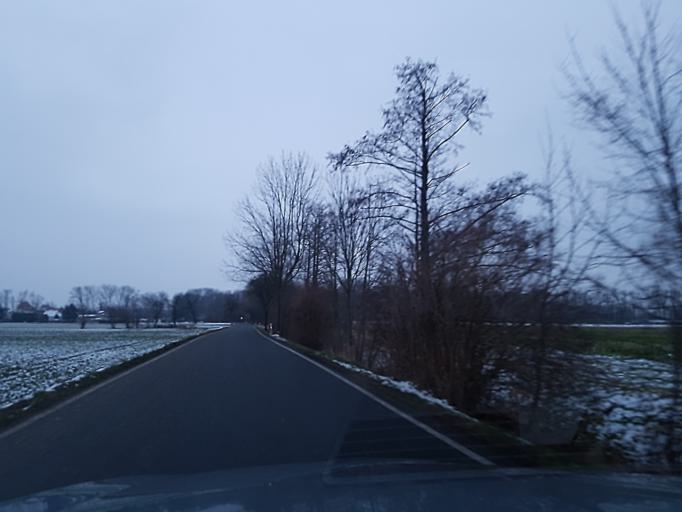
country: DE
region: Saxony
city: Stauchitz
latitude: 51.2510
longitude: 13.2055
